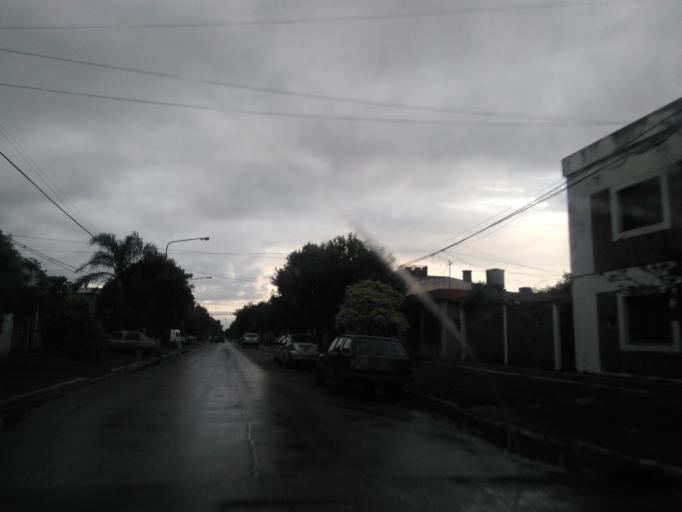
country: AR
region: Chaco
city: Resistencia
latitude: -27.4598
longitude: -58.9928
